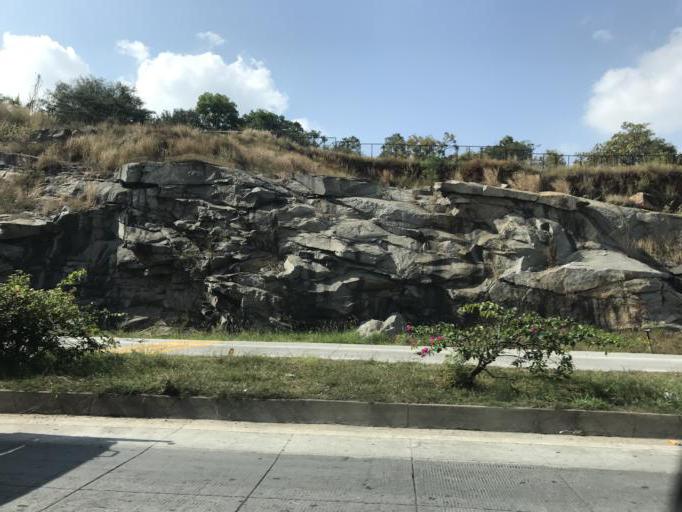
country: IN
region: Karnataka
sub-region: Bangalore Urban
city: Bangalore
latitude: 12.9109
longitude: 77.5300
